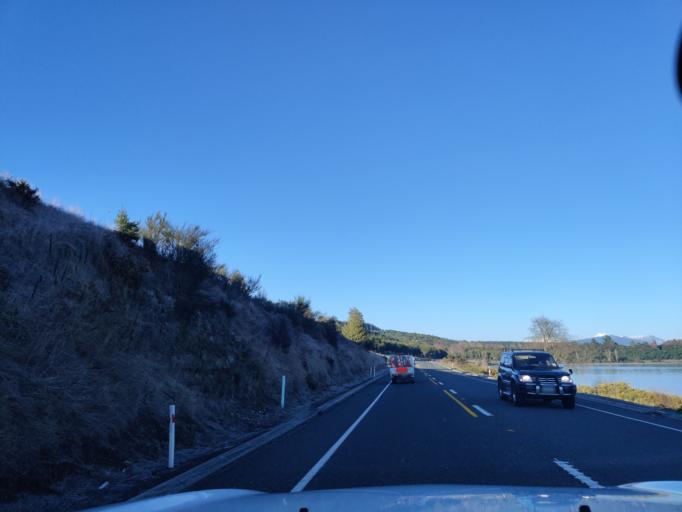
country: NZ
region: Waikato
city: Turangi
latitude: -38.8989
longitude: 175.9452
